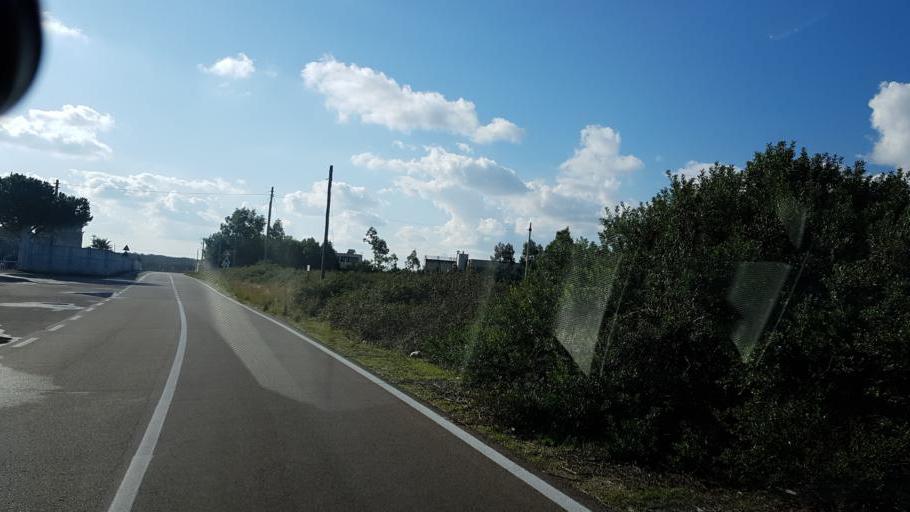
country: IT
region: Apulia
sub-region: Provincia di Lecce
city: Trepuzzi
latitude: 40.4443
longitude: 18.0959
